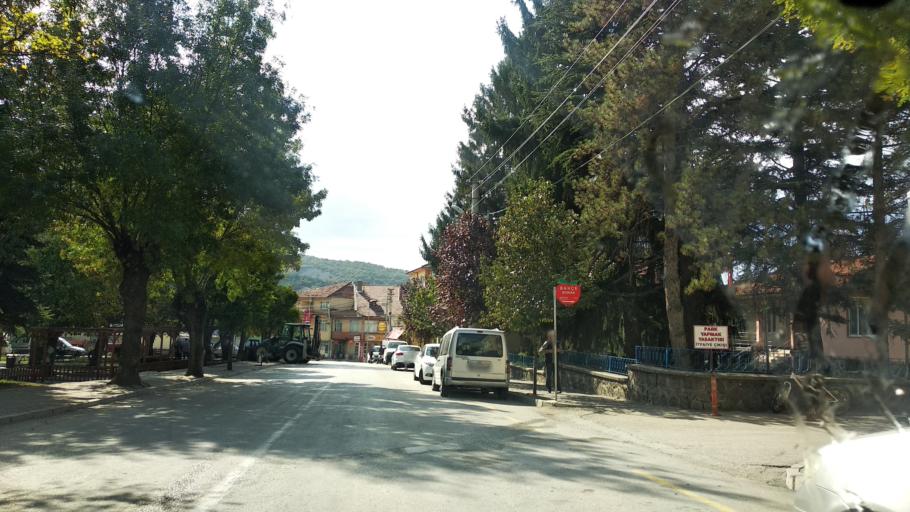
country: TR
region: Bolu
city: Seben
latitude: 40.4091
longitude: 31.5726
